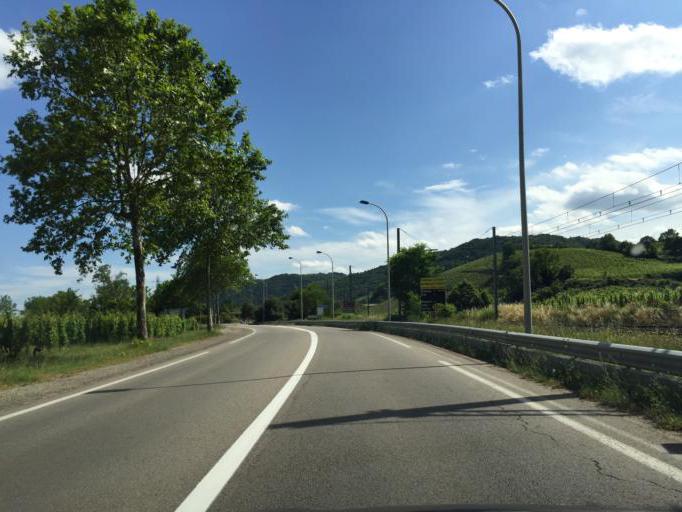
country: FR
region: Rhone-Alpes
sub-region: Departement de l'Ardeche
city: Mauves
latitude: 45.0479
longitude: 4.8296
